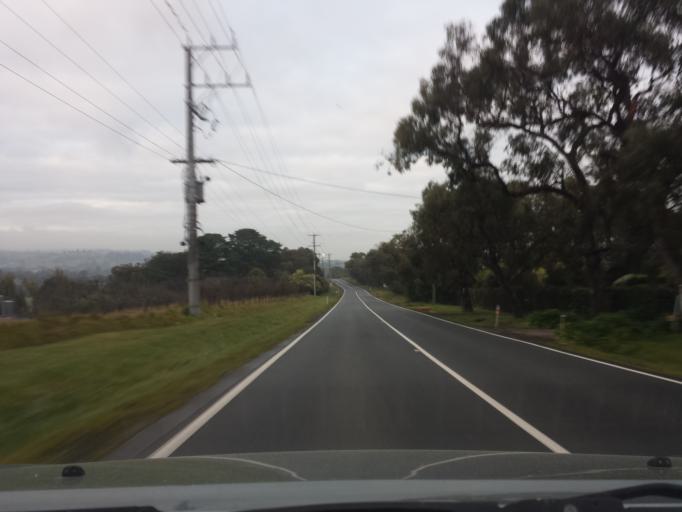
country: AU
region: Victoria
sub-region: Yarra Ranges
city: Belgrave South
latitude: -37.9445
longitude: 145.3545
